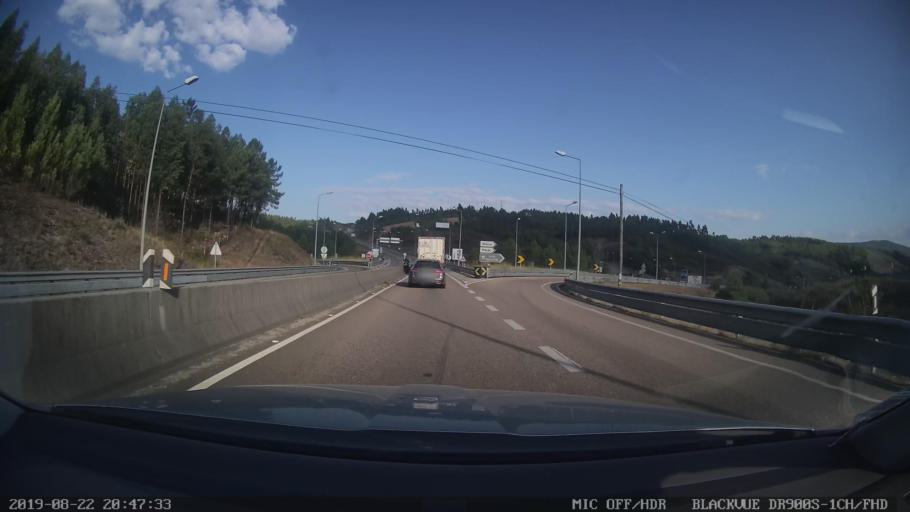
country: PT
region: Castelo Branco
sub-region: Proenca-A-Nova
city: Proenca-a-Nova
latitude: 39.7333
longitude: -7.8910
